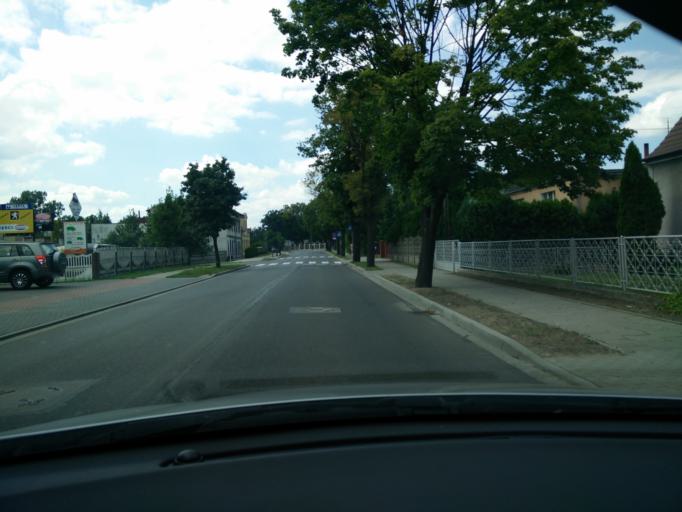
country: PL
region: Greater Poland Voivodeship
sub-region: Powiat sredzki
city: Sroda Wielkopolska
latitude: 52.2311
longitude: 17.2857
